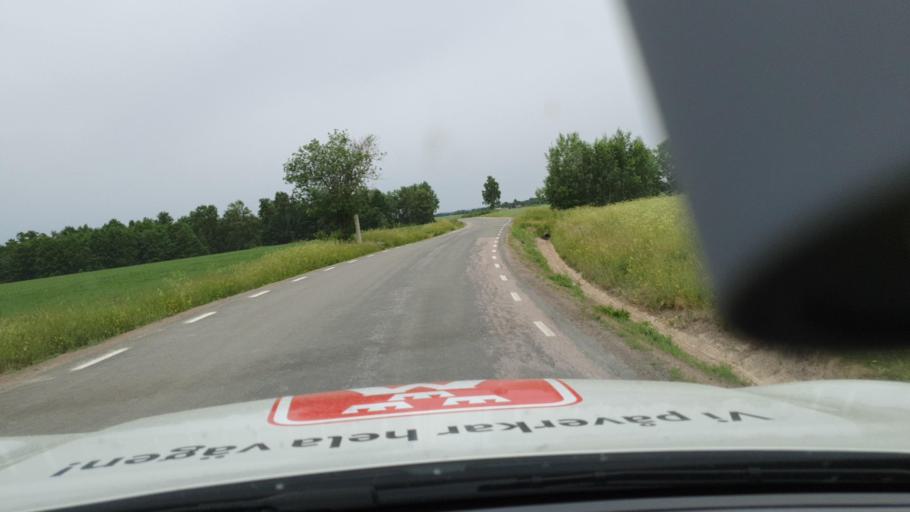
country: SE
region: Vaestra Goetaland
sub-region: Tidaholms Kommun
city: Olofstorp
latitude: 58.3073
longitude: 14.0637
